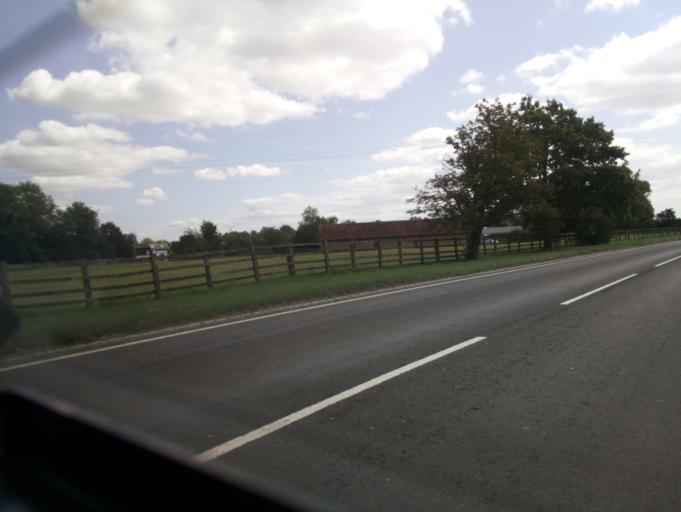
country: GB
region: England
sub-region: Buckinghamshire
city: Stone
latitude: 51.8408
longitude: -0.8781
